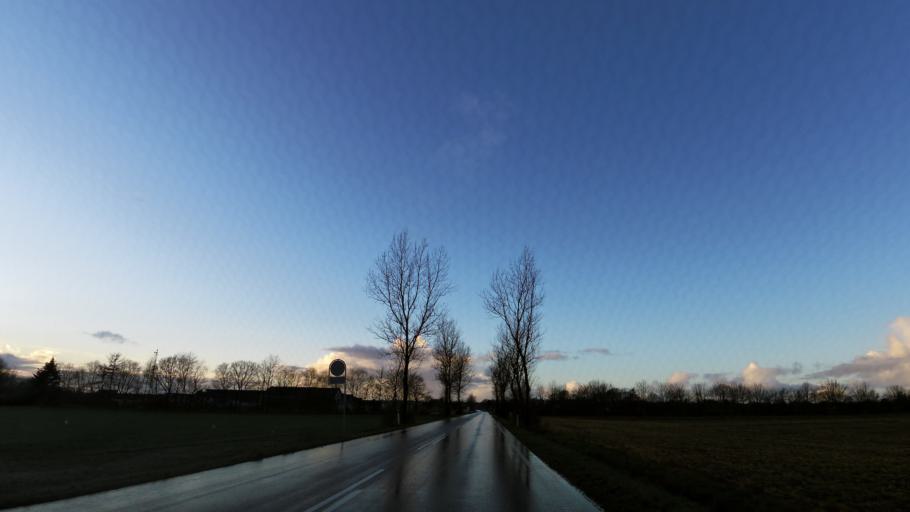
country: DK
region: Central Jutland
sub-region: Ikast-Brande Kommune
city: Brande
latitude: 56.0068
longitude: 9.1227
